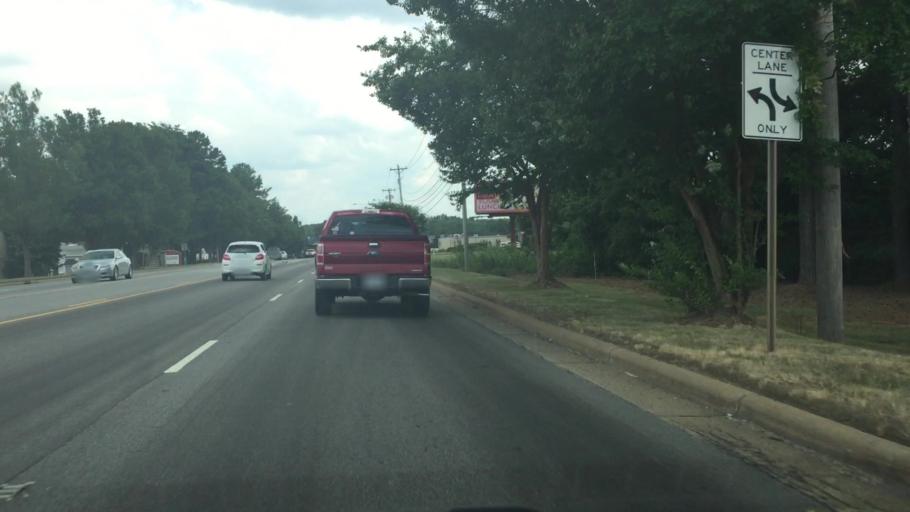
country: US
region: North Carolina
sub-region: Rowan County
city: Salisbury
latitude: 35.6811
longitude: -80.5065
